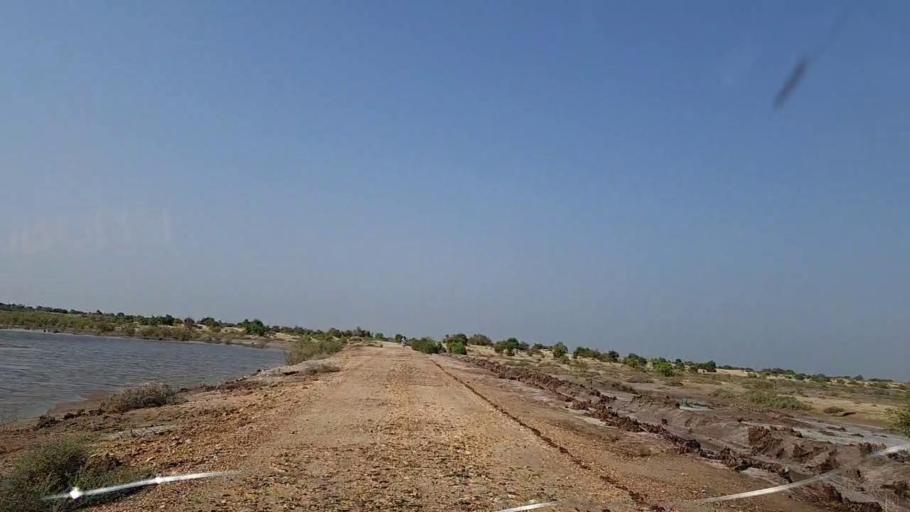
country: PK
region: Sindh
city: Khanpur
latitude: 27.6961
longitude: 69.3845
